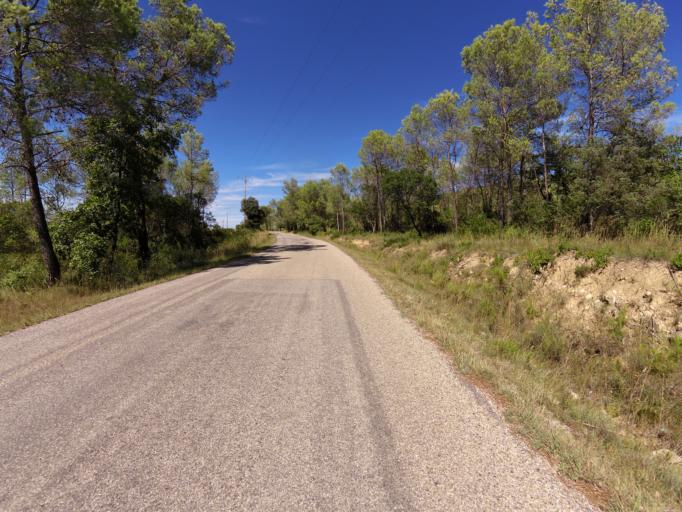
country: FR
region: Languedoc-Roussillon
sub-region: Departement du Gard
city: Quissac
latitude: 43.9105
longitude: 4.0470
